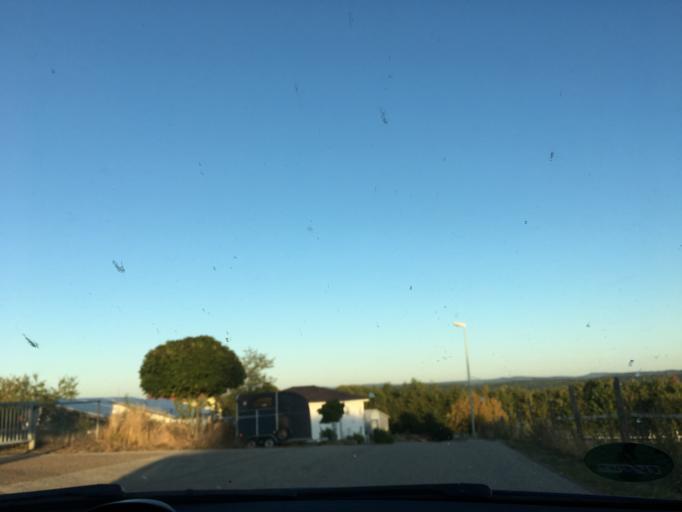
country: DE
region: Rheinland-Pfalz
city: Hermersberg
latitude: 49.3200
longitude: 7.6375
